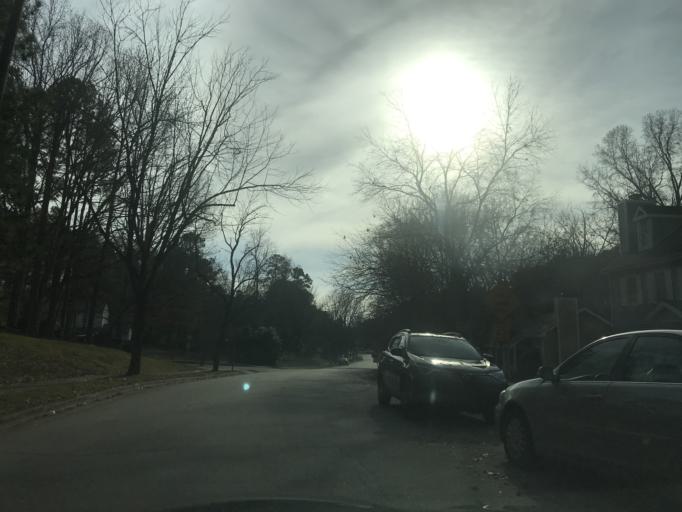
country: US
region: North Carolina
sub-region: Wake County
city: Raleigh
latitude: 35.8307
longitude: -78.5896
